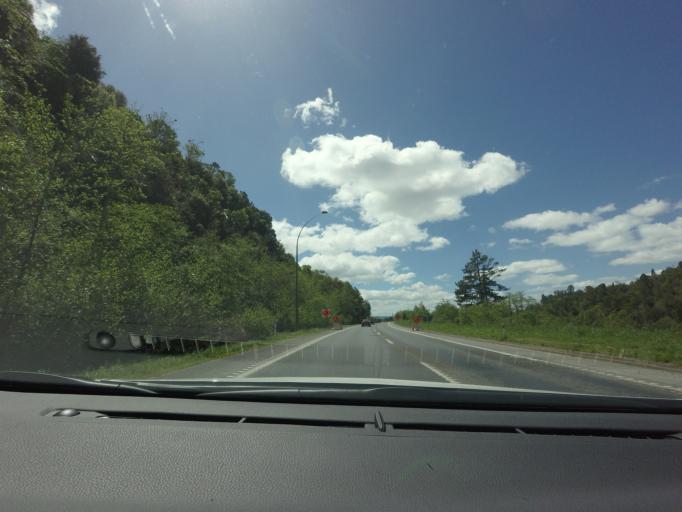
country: NZ
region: Bay of Plenty
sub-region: Rotorua District
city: Rotorua
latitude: -38.1718
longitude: 176.2457
